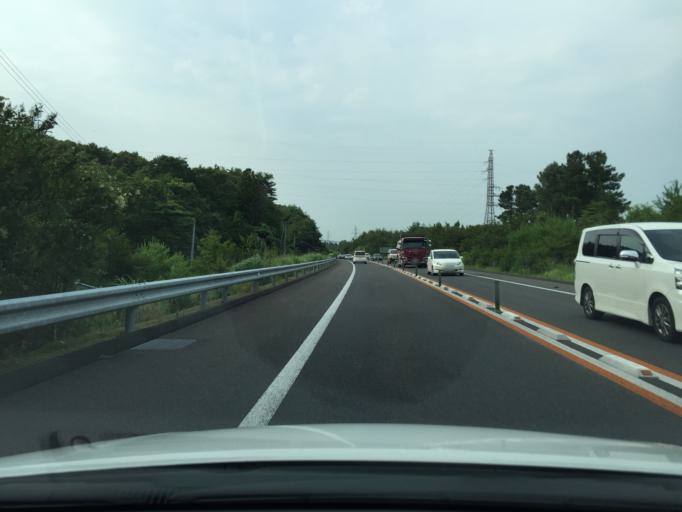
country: JP
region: Fukushima
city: Namie
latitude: 37.2568
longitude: 140.9914
